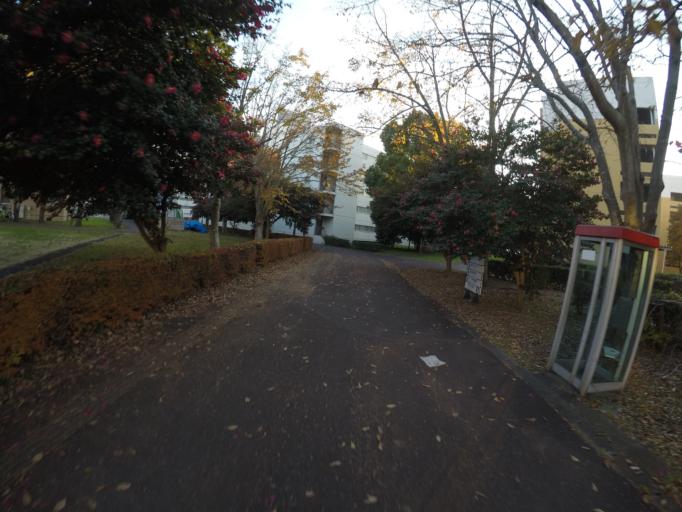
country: JP
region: Ibaraki
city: Naka
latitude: 36.0948
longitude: 140.1044
